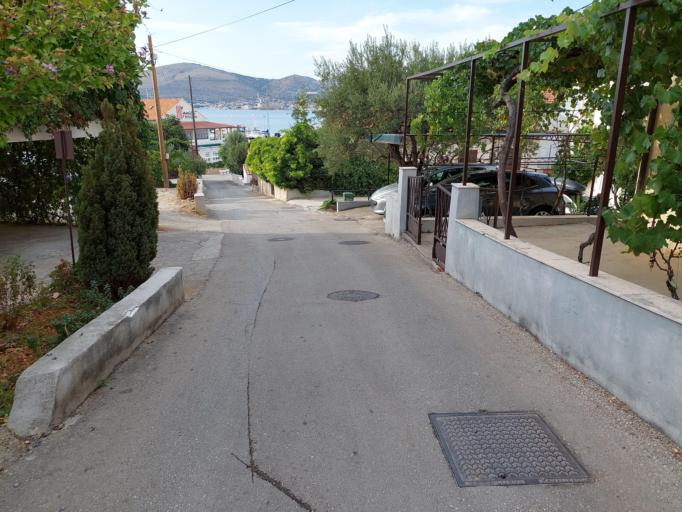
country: HR
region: Splitsko-Dalmatinska
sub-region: Grad Trogir
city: Trogir
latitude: 43.4950
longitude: 16.2612
